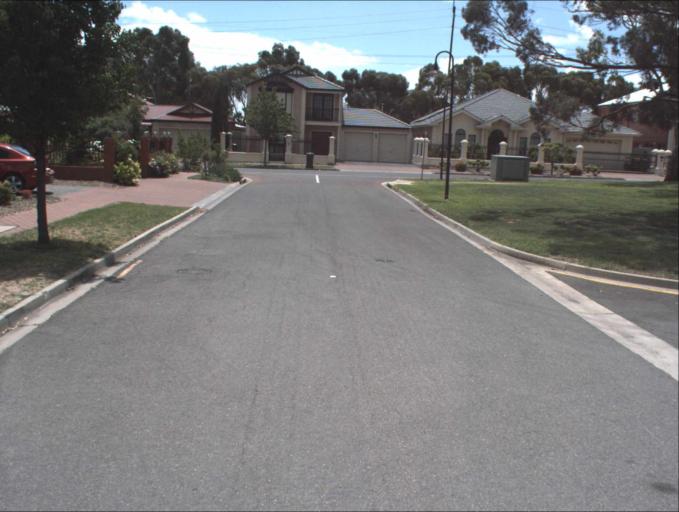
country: AU
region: South Australia
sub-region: Salisbury
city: Ingle Farm
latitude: -34.8484
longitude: 138.6275
